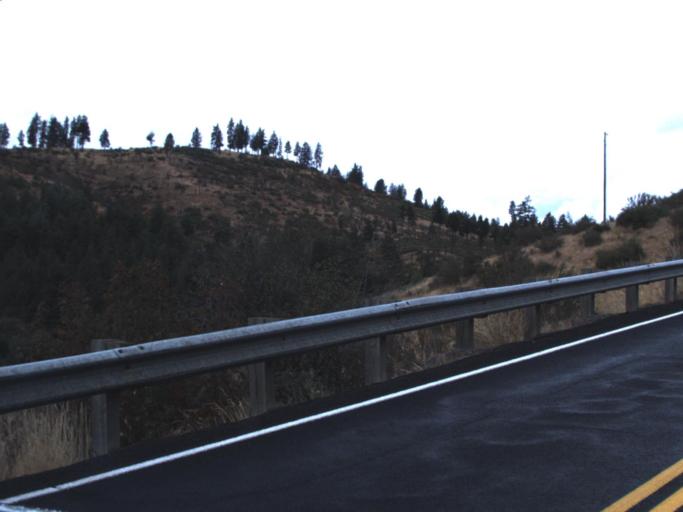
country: US
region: Washington
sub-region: Lincoln County
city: Davenport
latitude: 47.7717
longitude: -117.8933
